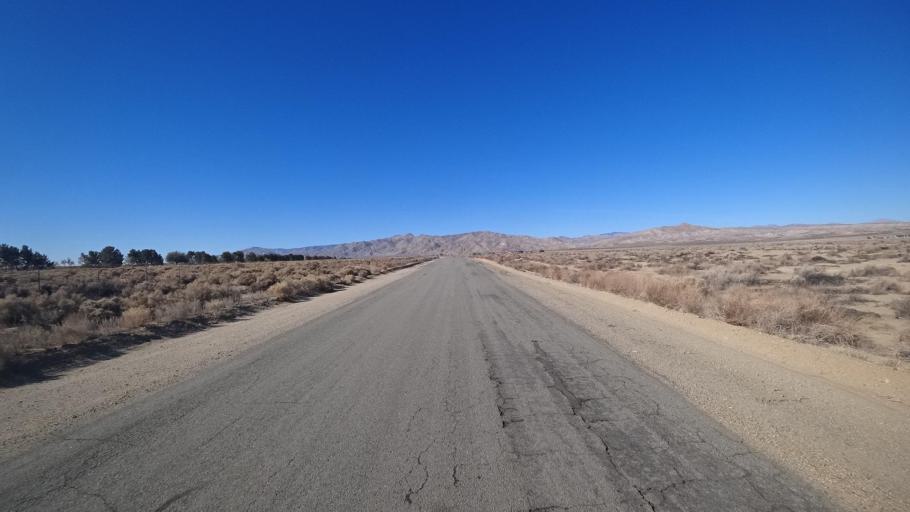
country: US
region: California
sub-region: Kern County
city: California City
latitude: 35.2868
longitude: -117.9554
